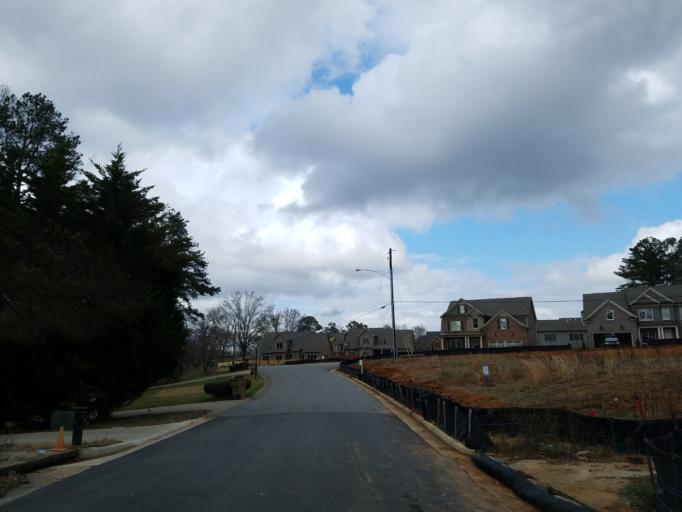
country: US
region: Georgia
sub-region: Cobb County
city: Marietta
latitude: 34.0156
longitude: -84.5026
